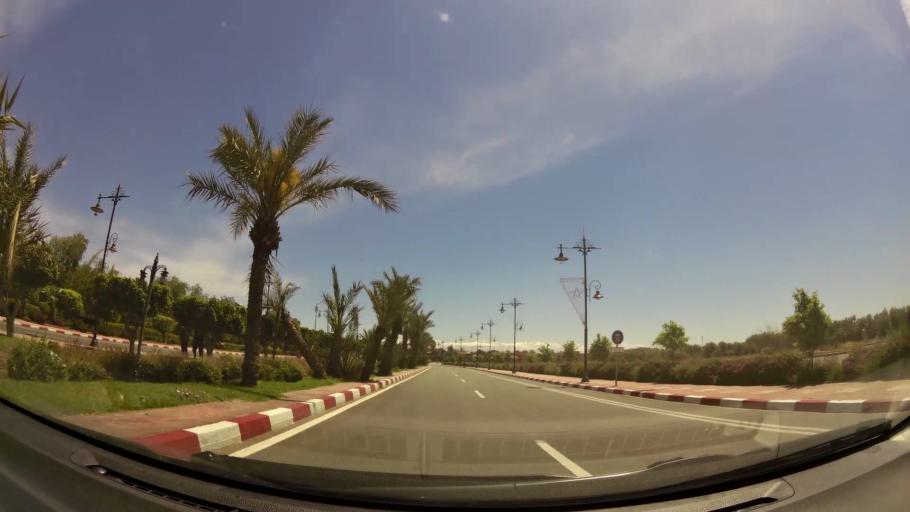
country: MA
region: Marrakech-Tensift-Al Haouz
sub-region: Marrakech
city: Marrakesh
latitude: 31.6161
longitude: -7.9964
